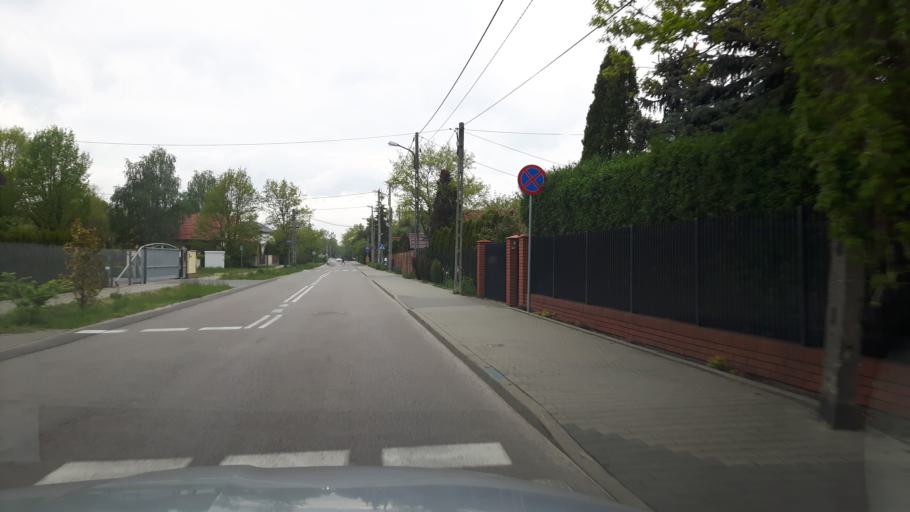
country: PL
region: Masovian Voivodeship
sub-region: Warszawa
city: Rembertow
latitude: 52.2692
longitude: 21.1627
